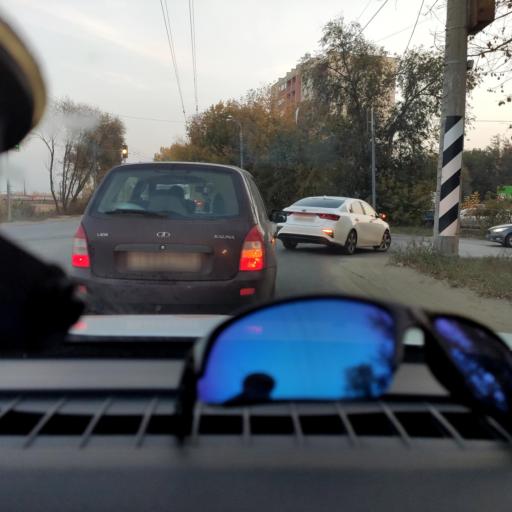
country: RU
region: Samara
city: Samara
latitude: 53.1570
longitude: 50.0912
